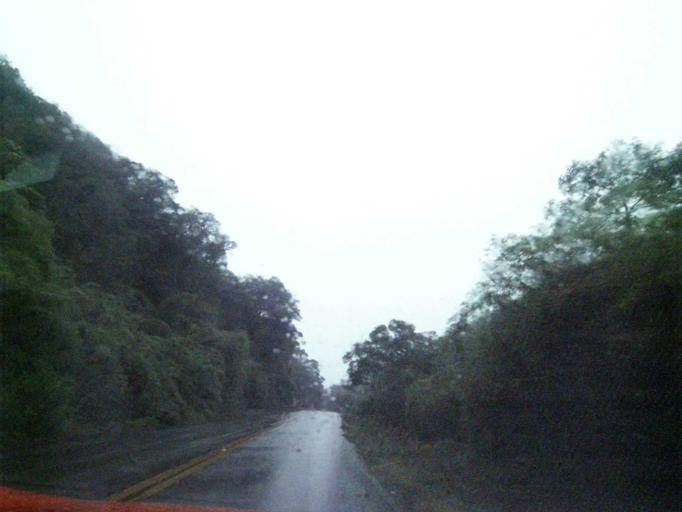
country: BR
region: Santa Catarina
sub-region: Anitapolis
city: Anitapolis
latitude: -27.7647
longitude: -49.0391
